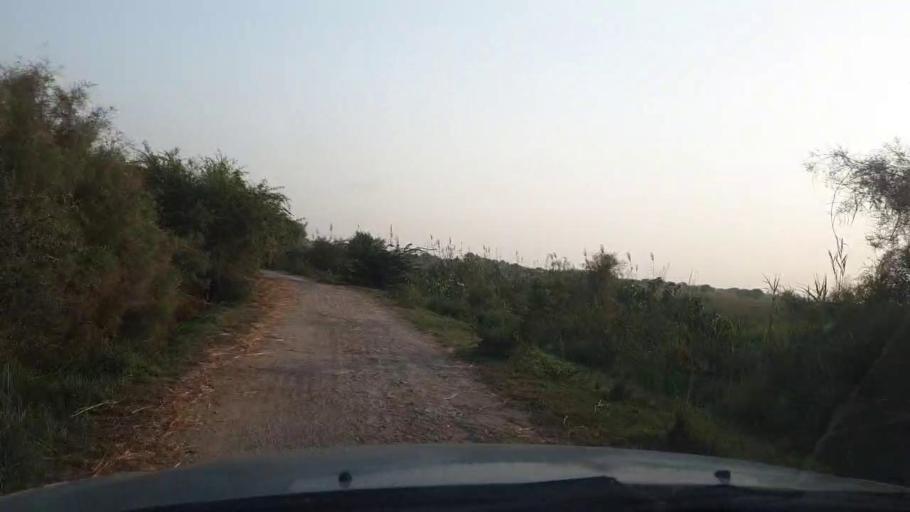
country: PK
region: Sindh
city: Tando Muhammad Khan
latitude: 24.9986
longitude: 68.4313
